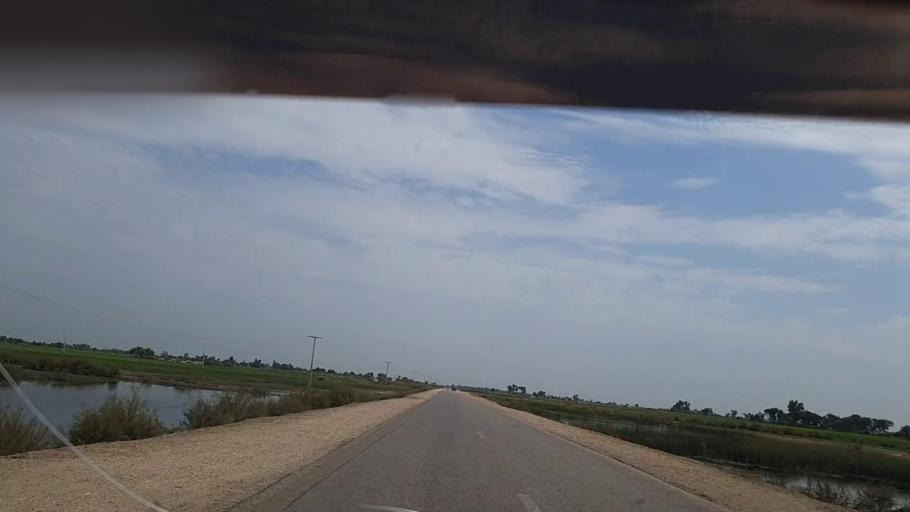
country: PK
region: Sindh
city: Thul
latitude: 28.1948
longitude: 68.7930
